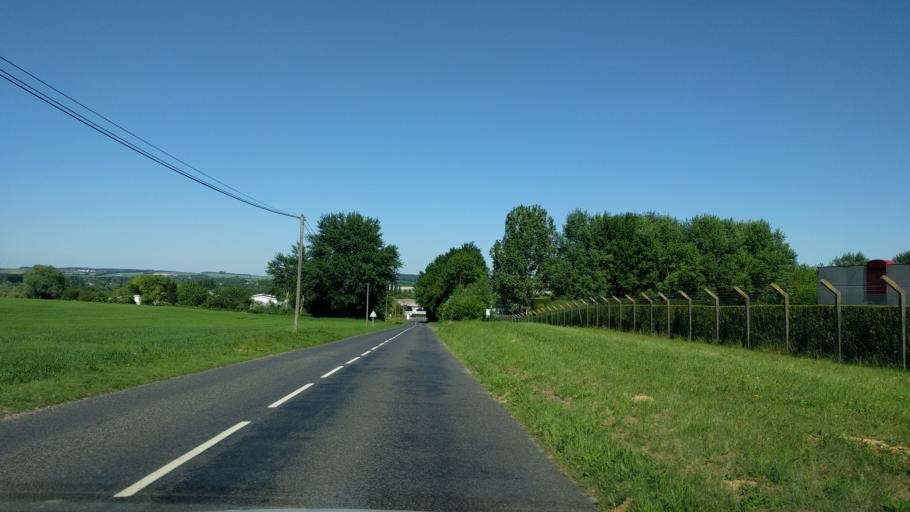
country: FR
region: Picardie
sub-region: Departement de la Somme
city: Peronne
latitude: 49.9134
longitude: 2.9221
